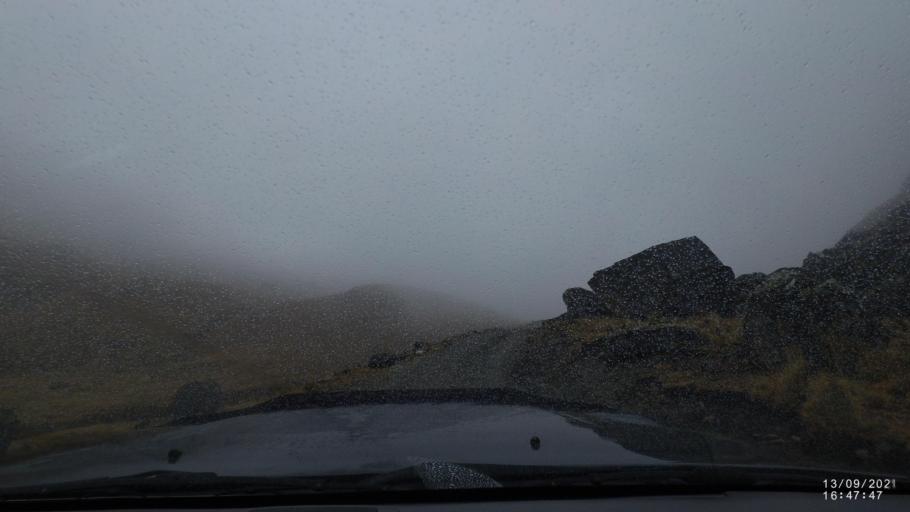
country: BO
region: Cochabamba
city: Colomi
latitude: -17.2983
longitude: -65.7063
